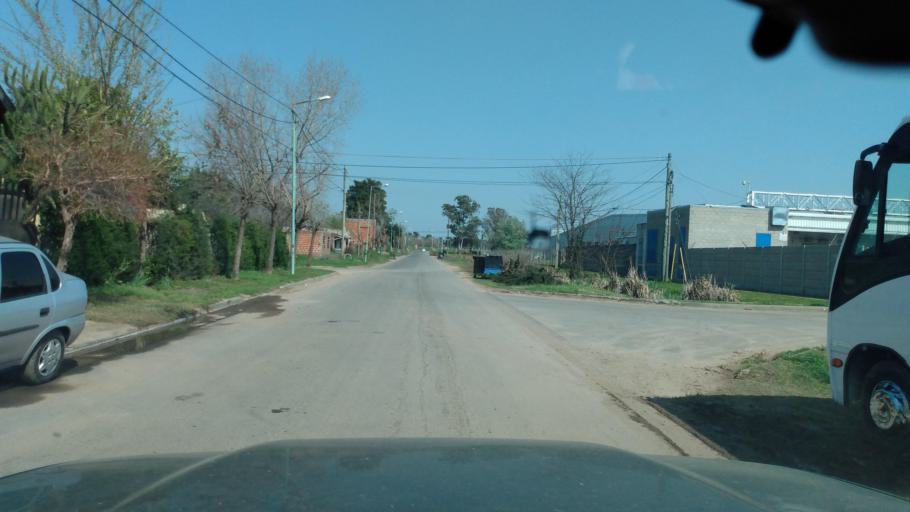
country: AR
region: Buenos Aires
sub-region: Partido de Lujan
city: Lujan
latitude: -34.5474
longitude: -59.1093
